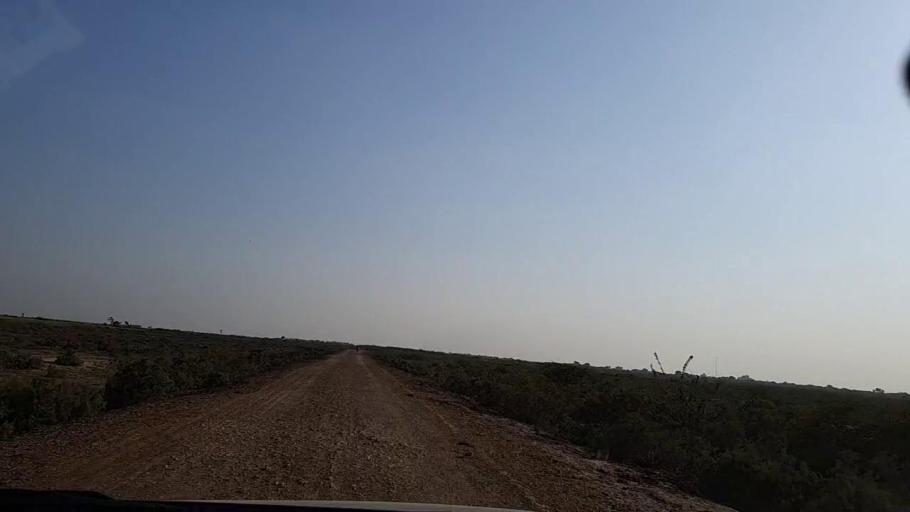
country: PK
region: Sindh
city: Mirwah Gorchani
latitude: 25.2262
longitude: 68.9731
